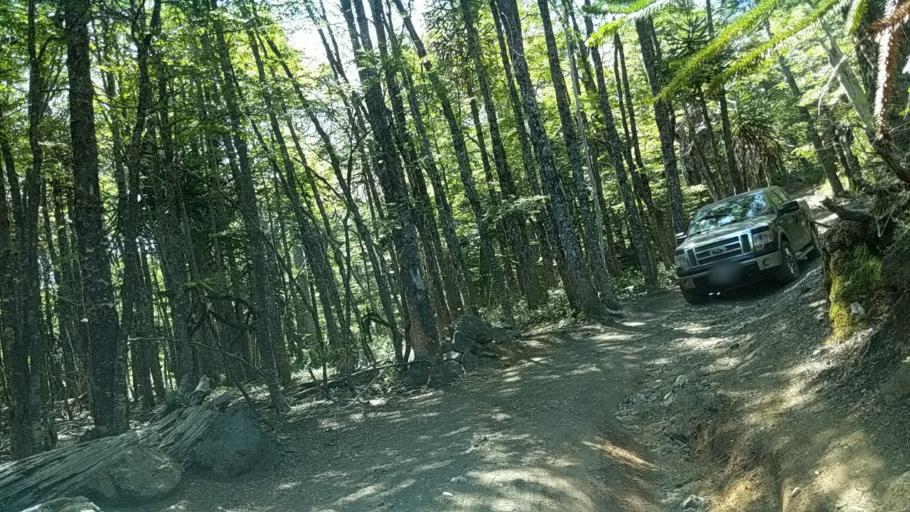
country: CL
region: Araucania
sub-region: Provincia de Cautin
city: Pucon
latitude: -39.4610
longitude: -71.8524
